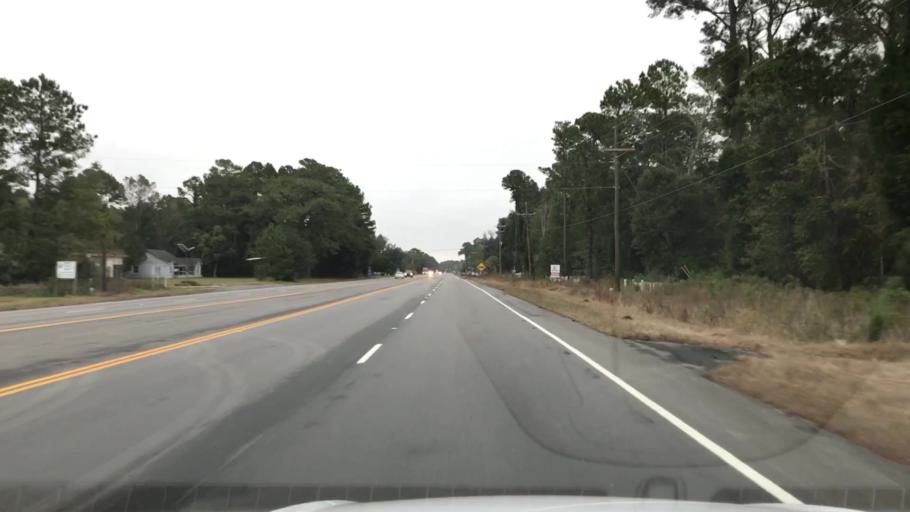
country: US
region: South Carolina
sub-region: Charleston County
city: Awendaw
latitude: 33.0900
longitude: -79.4842
